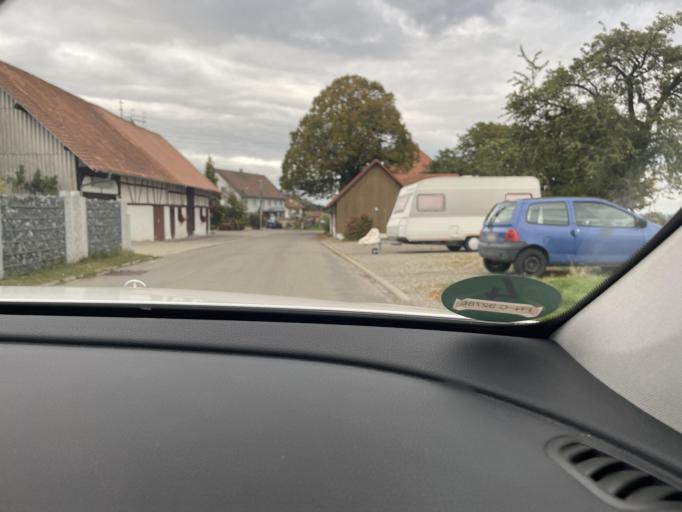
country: DE
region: Baden-Wuerttemberg
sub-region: Tuebingen Region
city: Wilhelmsdorf
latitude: 47.8119
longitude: 9.4159
